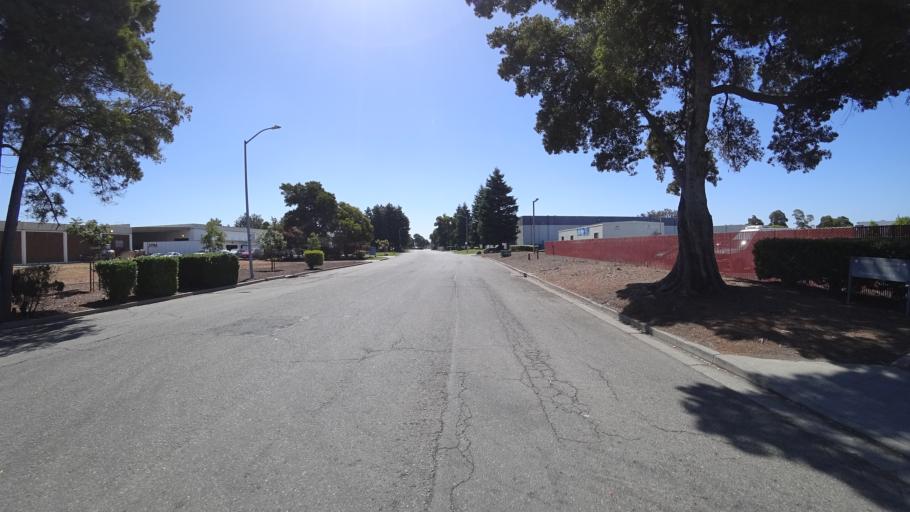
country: US
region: California
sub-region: Alameda County
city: San Lorenzo
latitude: 37.6586
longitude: -122.1290
